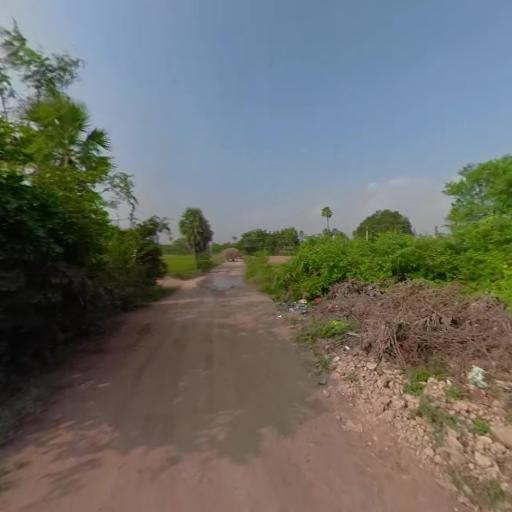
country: IN
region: Telangana
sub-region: Nalgonda
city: Suriapet
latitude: 17.2012
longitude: 79.4876
